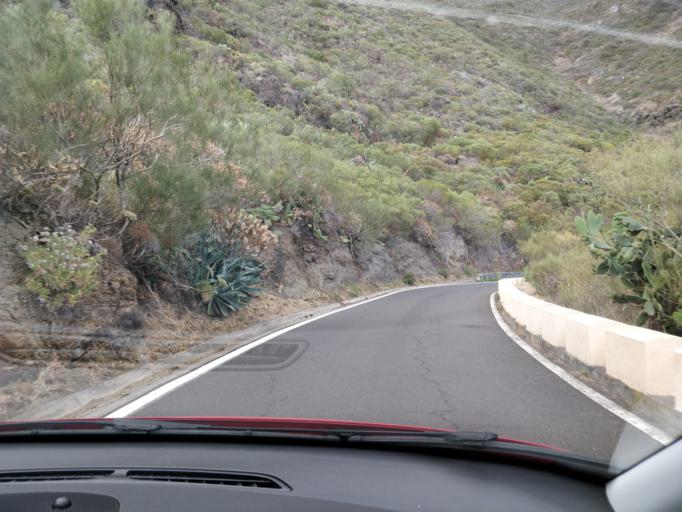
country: ES
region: Canary Islands
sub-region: Provincia de Santa Cruz de Tenerife
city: Santiago del Teide
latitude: 28.3167
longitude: -16.8514
